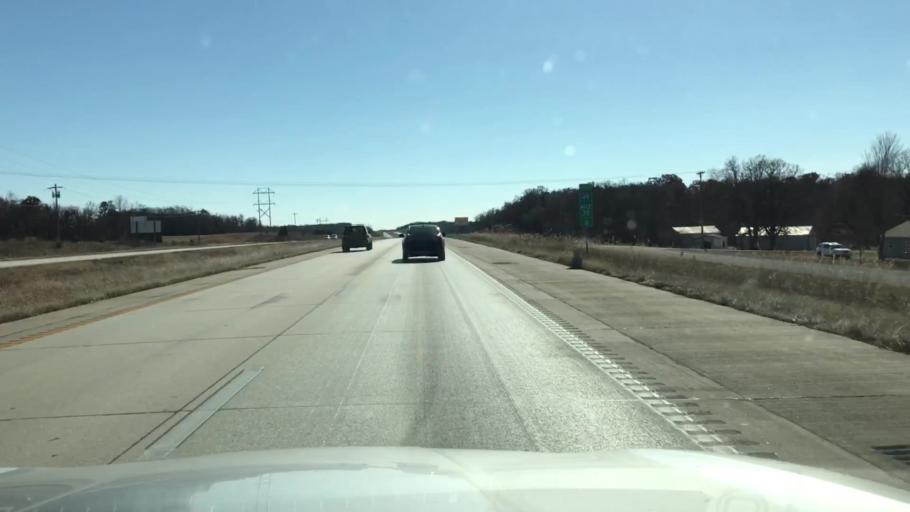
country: US
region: Missouri
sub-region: Jasper County
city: Duenweg
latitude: 37.0409
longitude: -94.4285
